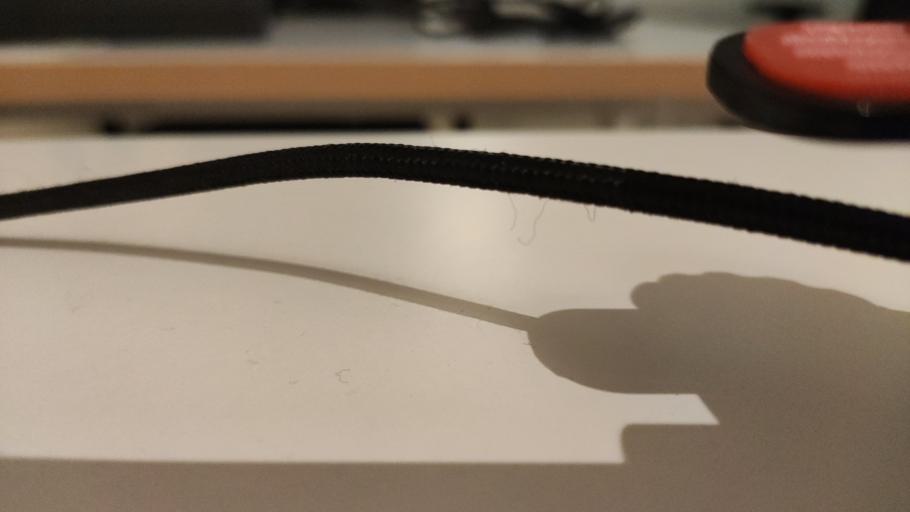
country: RU
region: Moskovskaya
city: Budenovetc
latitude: 56.3933
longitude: 37.6316
